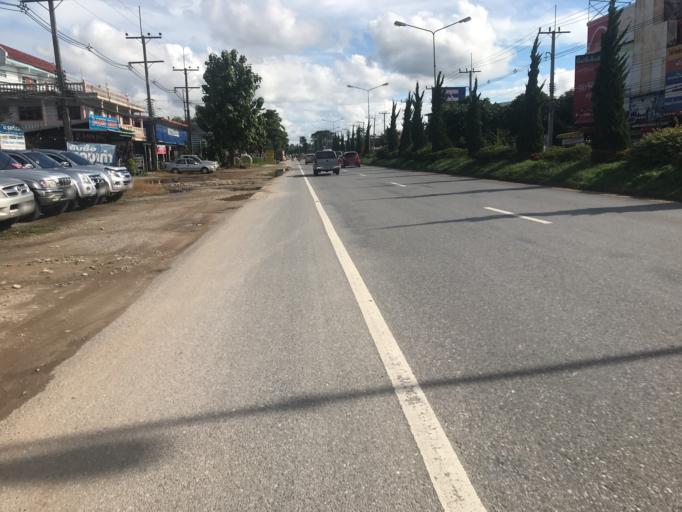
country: TH
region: Chiang Rai
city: Chiang Rai
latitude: 19.9527
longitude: 99.8500
